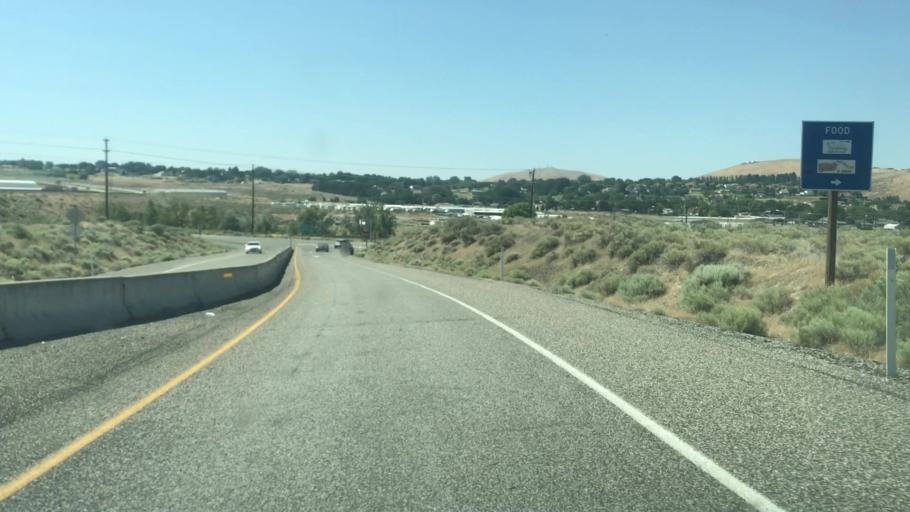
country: US
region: Washington
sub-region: Benton County
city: Richland
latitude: 46.1944
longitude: -119.2648
